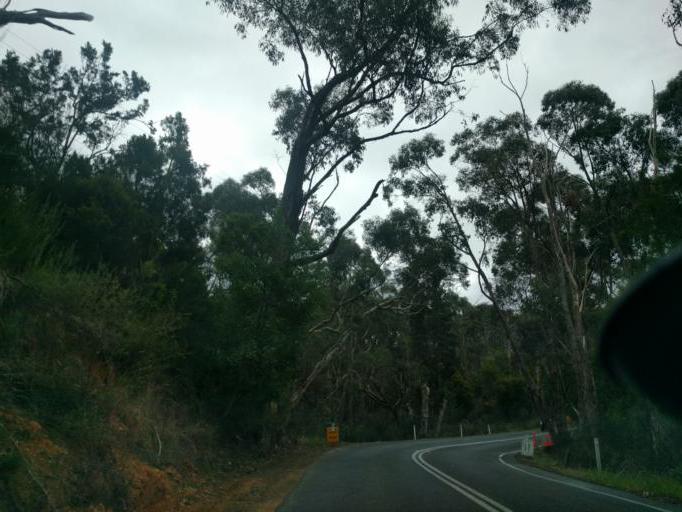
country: AU
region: South Australia
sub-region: Adelaide Hills
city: Stirling
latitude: -35.0283
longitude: 138.7647
